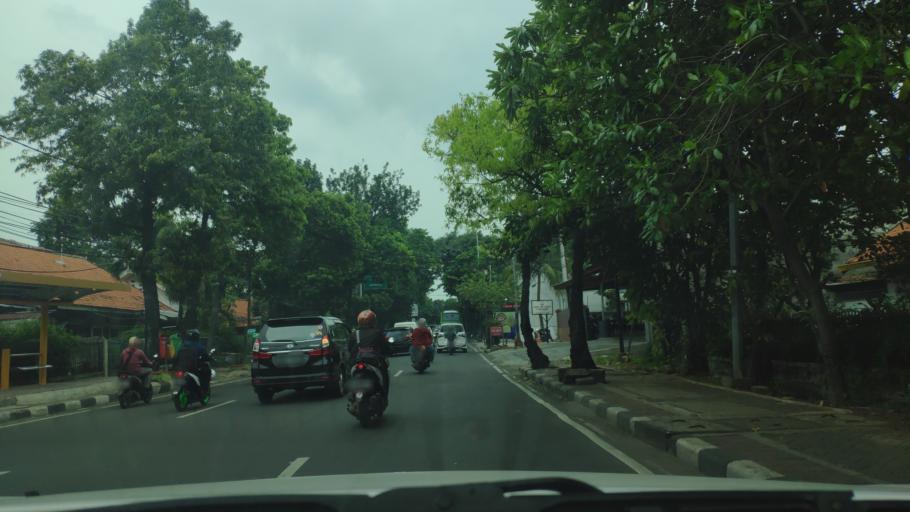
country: ID
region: Jakarta Raya
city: Jakarta
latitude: -6.1885
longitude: 106.7854
